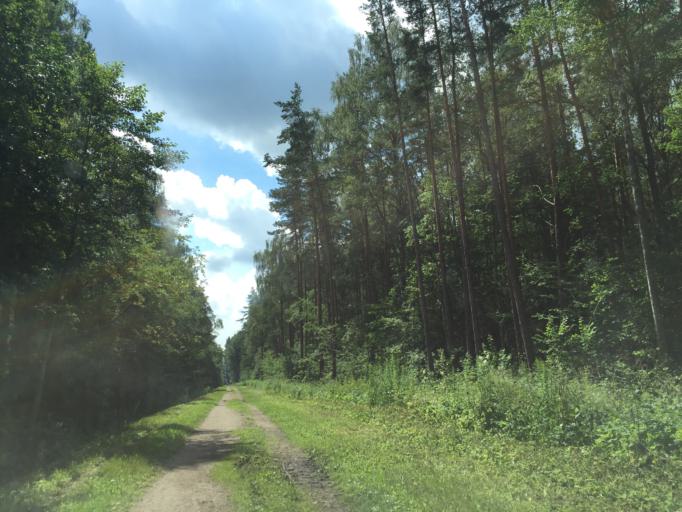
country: LV
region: Ozolnieku
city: Ozolnieki
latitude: 56.6790
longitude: 23.7531
